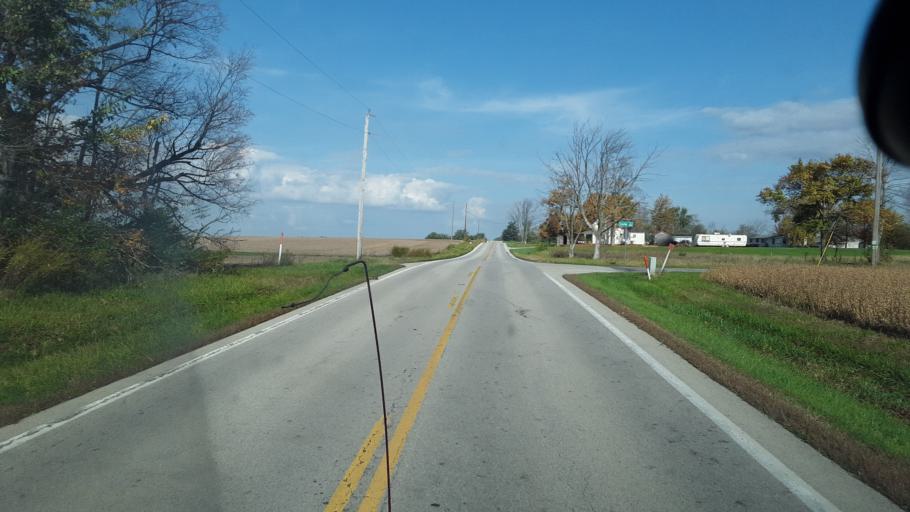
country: US
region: Ohio
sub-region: Clinton County
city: Sabina
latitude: 39.5177
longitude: -83.6934
